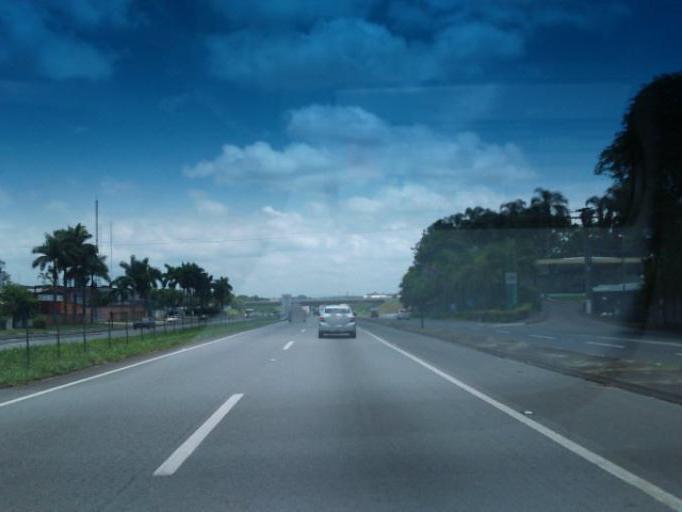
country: BR
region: Sao Paulo
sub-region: Registro
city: Registro
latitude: -24.5051
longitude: -47.8481
